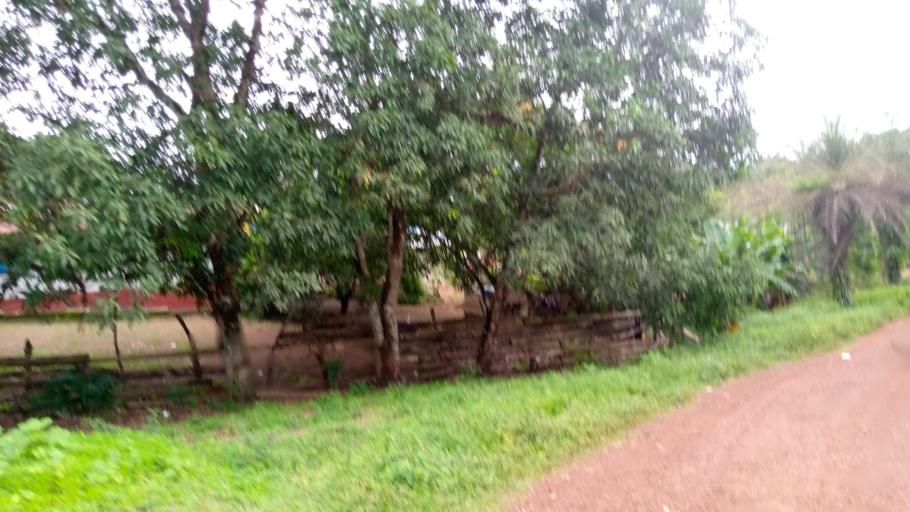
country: SL
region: Southern Province
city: Moyamba
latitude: 8.1646
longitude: -12.4398
